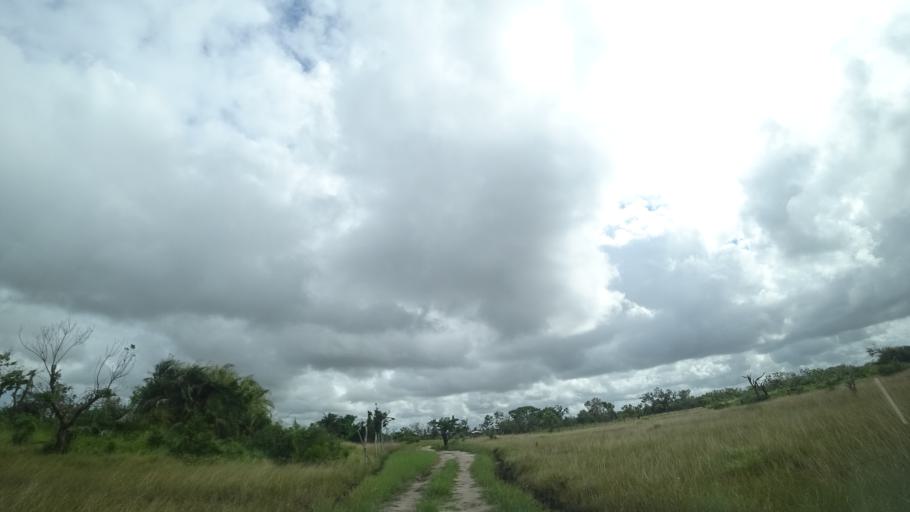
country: MZ
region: Sofala
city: Beira
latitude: -19.6120
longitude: 35.2175
